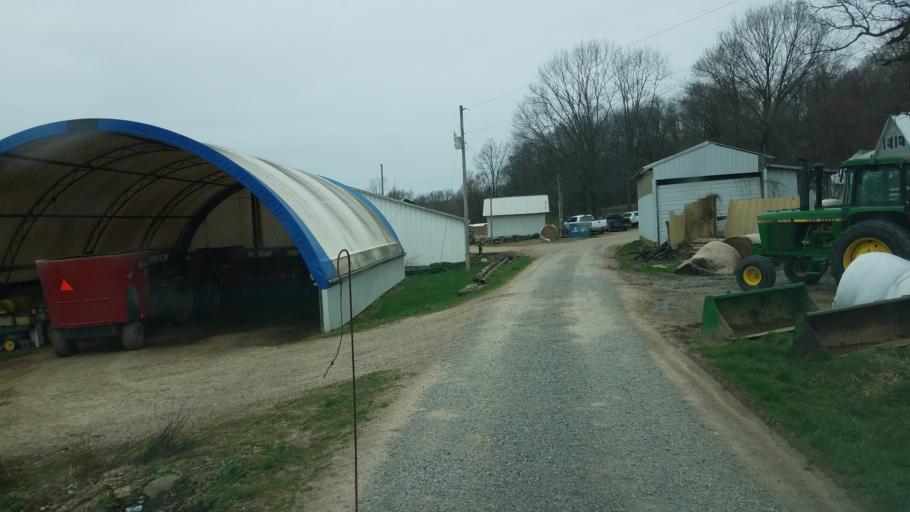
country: US
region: Ohio
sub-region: Knox County
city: Mount Vernon
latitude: 40.4575
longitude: -82.4513
